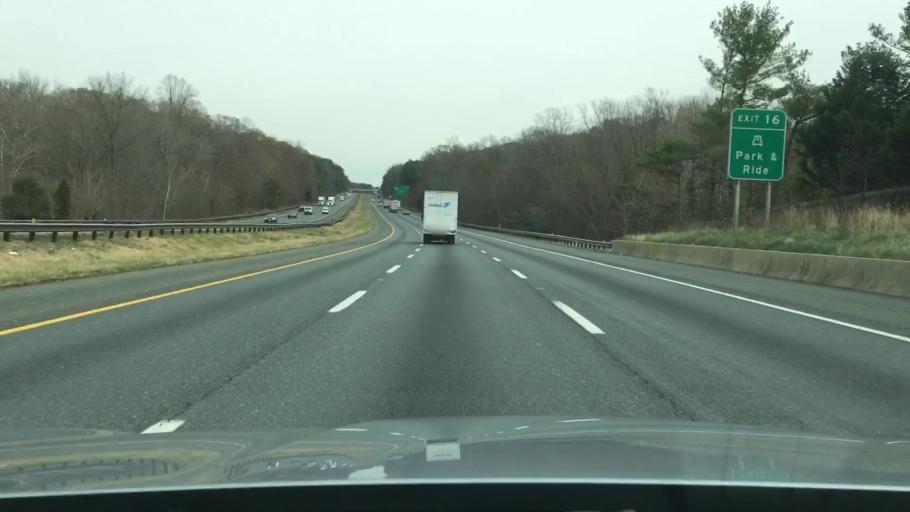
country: US
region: Maryland
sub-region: Anne Arundel County
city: Crofton
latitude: 38.9562
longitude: -76.6762
